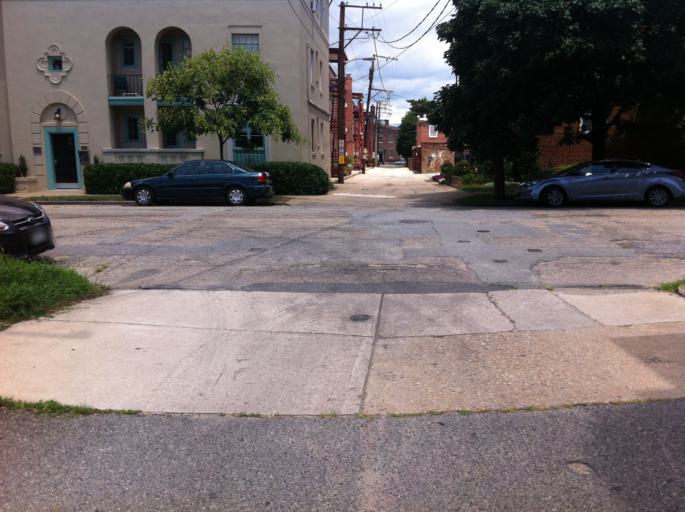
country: US
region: Virginia
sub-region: City of Richmond
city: Richmond
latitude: 37.5580
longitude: -77.4719
